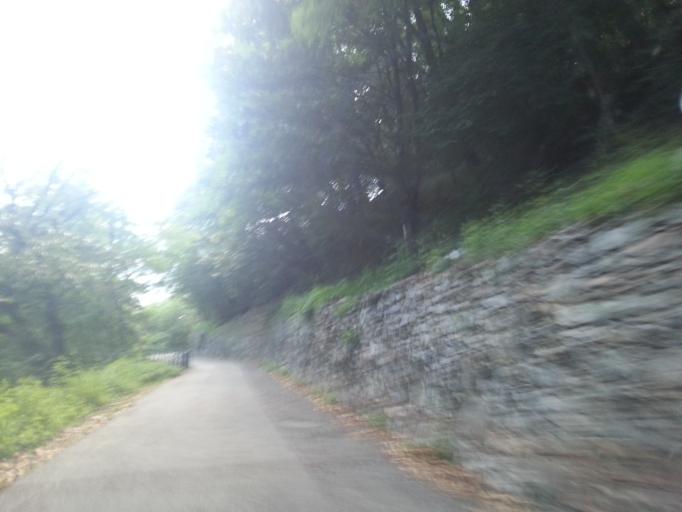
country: IT
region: Lombardy
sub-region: Provincia di Como
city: Sorico
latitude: 46.1804
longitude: 9.3833
